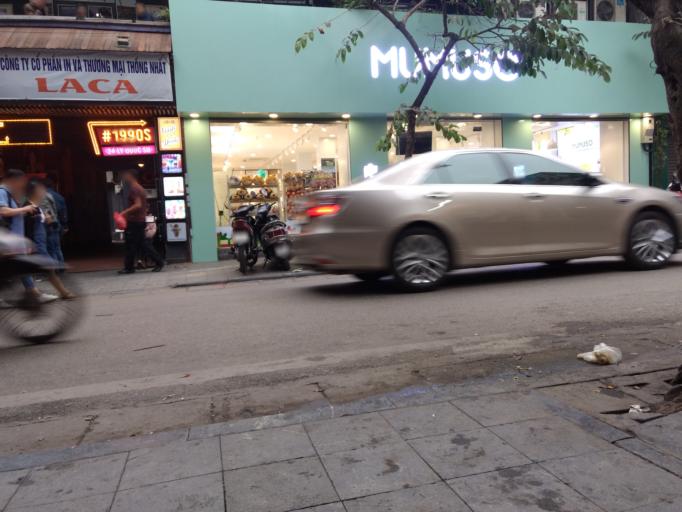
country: VN
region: Ha Noi
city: Hoan Kiem
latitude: 21.0300
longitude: 105.8491
